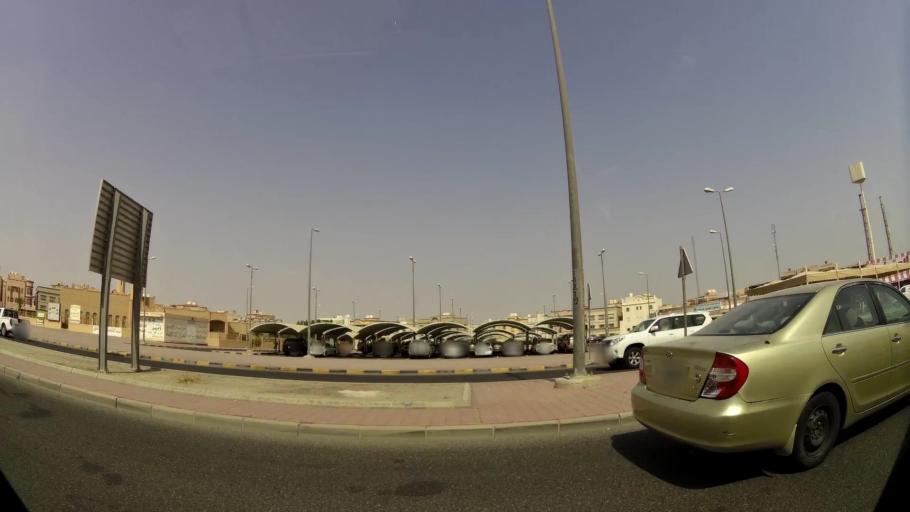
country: KW
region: Muhafazat al Jahra'
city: Al Jahra'
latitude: 29.3066
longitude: 47.6952
